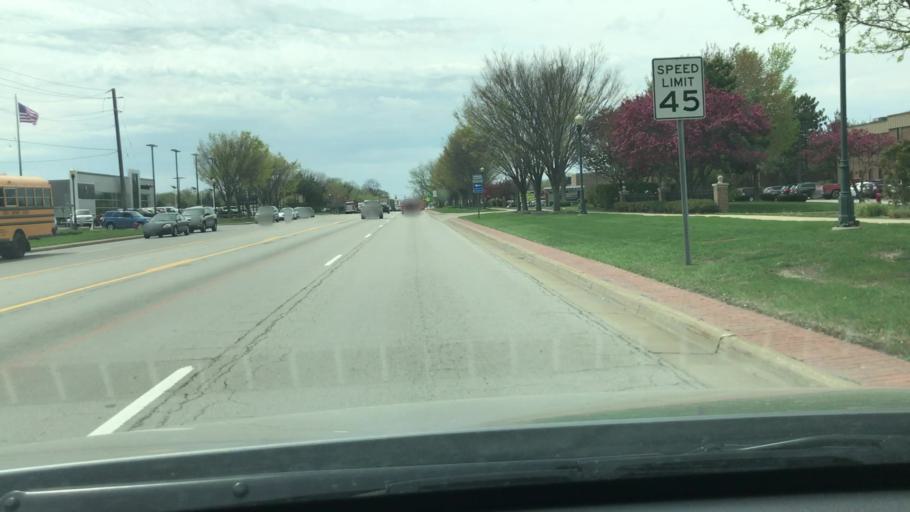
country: US
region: Michigan
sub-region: Wayne County
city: Plymouth
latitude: 42.3595
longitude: -83.4404
